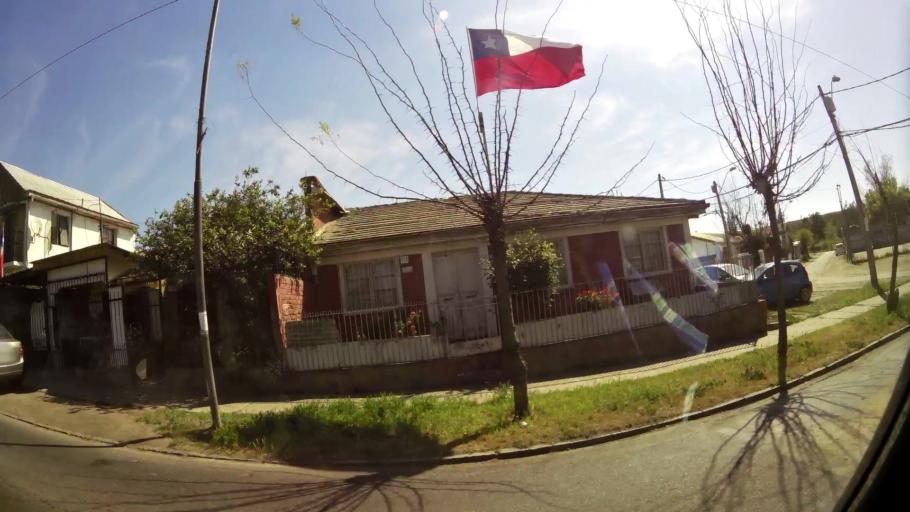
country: CL
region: Santiago Metropolitan
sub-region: Provincia de Santiago
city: Lo Prado
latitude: -33.4942
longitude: -70.7277
